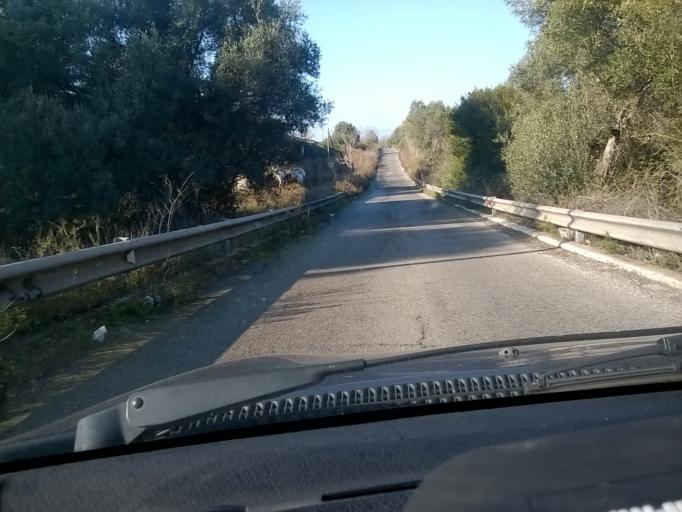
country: IT
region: Apulia
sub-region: Provincia di Taranto
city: Paolo VI
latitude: 40.4665
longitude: 17.2870
